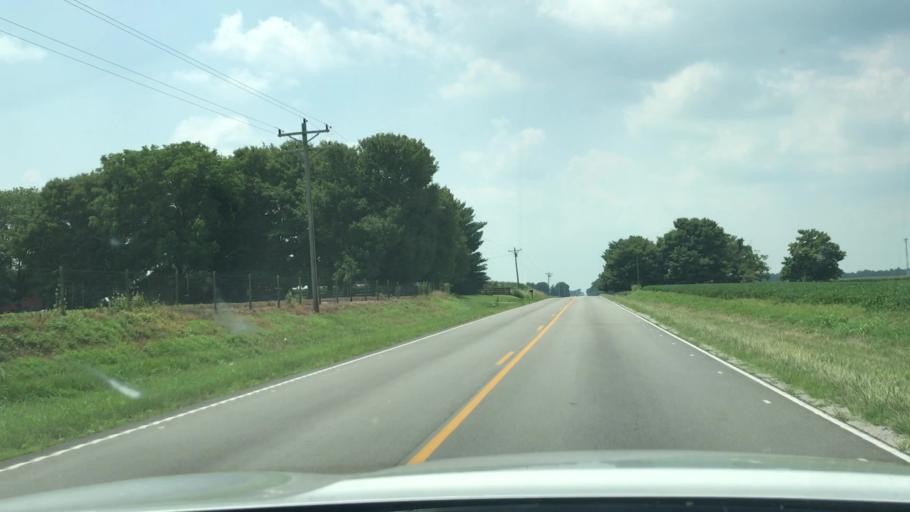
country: US
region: Kentucky
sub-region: Todd County
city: Guthrie
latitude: 36.7009
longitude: -87.1159
